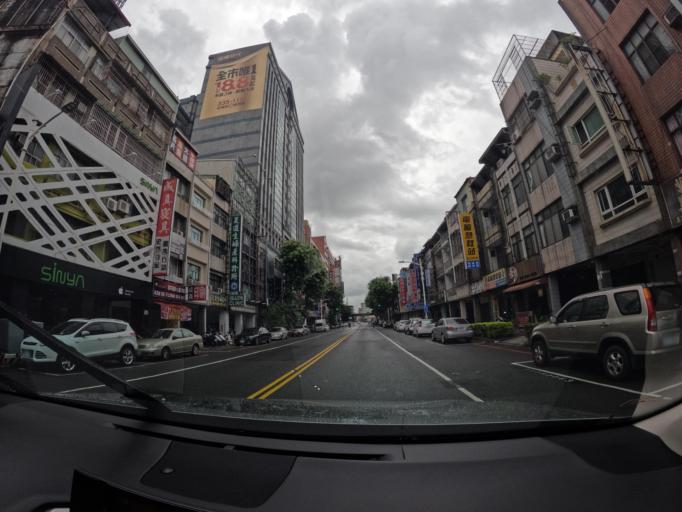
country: TW
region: Kaohsiung
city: Kaohsiung
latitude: 22.6374
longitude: 120.3113
